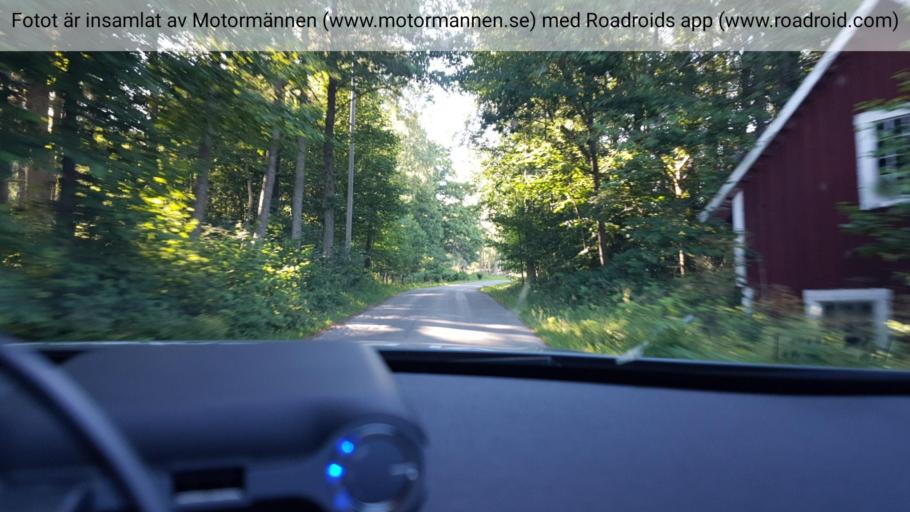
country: SE
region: Joenkoeping
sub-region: Habo Kommun
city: Habo
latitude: 58.0519
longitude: 14.1841
